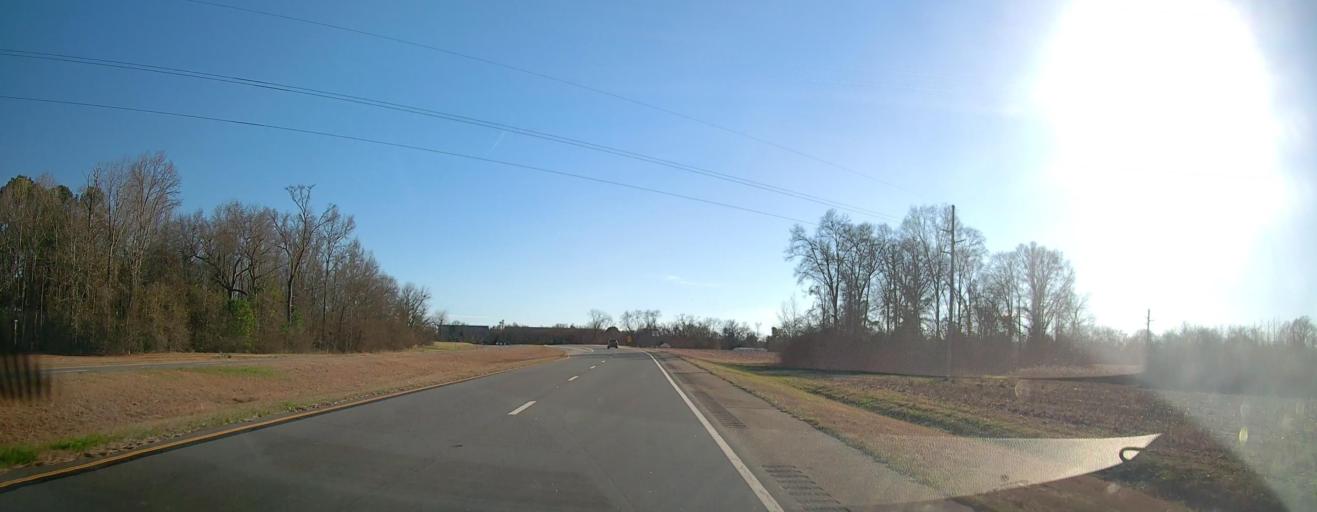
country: US
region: Georgia
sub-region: Sumter County
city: Americus
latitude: 31.9051
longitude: -84.2617
